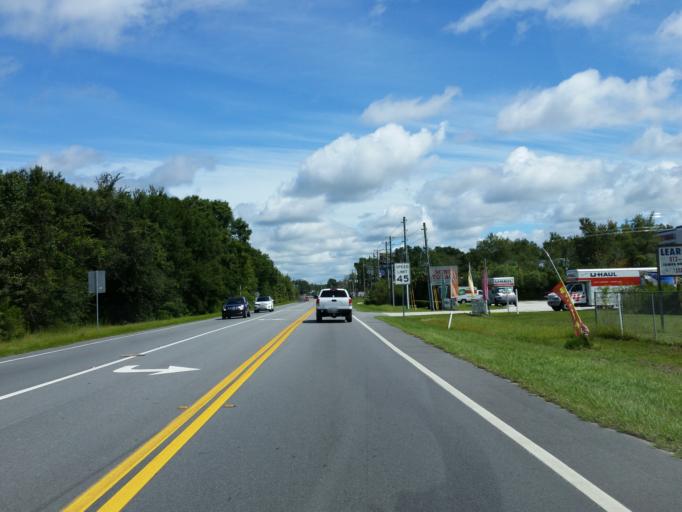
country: US
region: Florida
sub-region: Pasco County
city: Wesley Chapel
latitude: 28.2257
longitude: -82.3788
